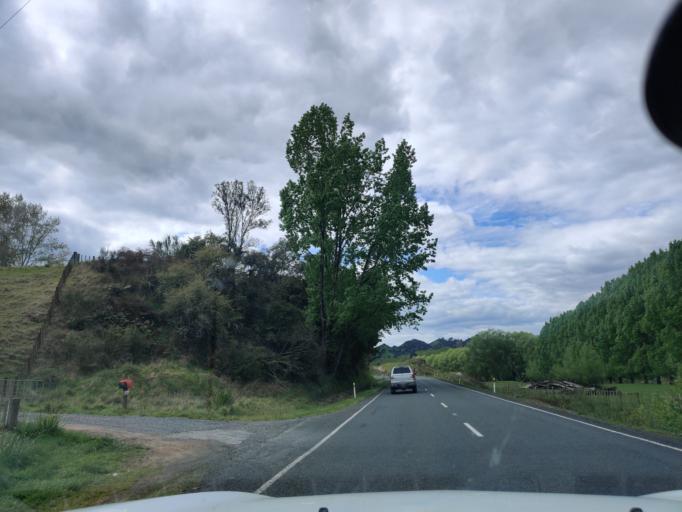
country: NZ
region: Waikato
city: Turangi
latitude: -38.8486
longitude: 175.2345
